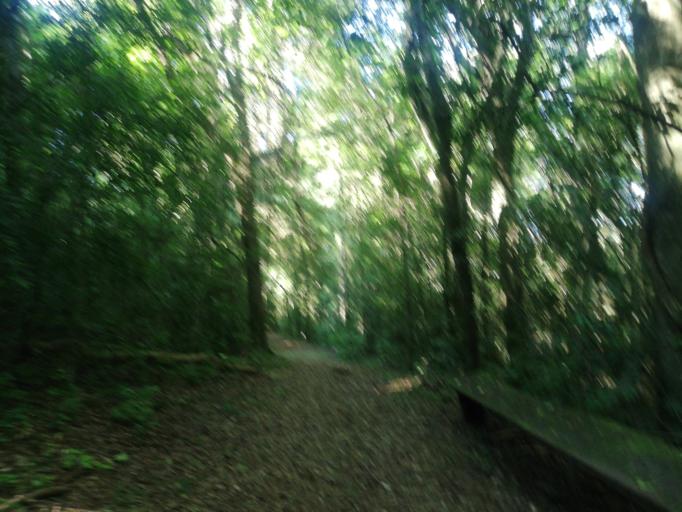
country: AR
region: Misiones
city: Cerro Azul
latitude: -27.7503
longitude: -55.5612
